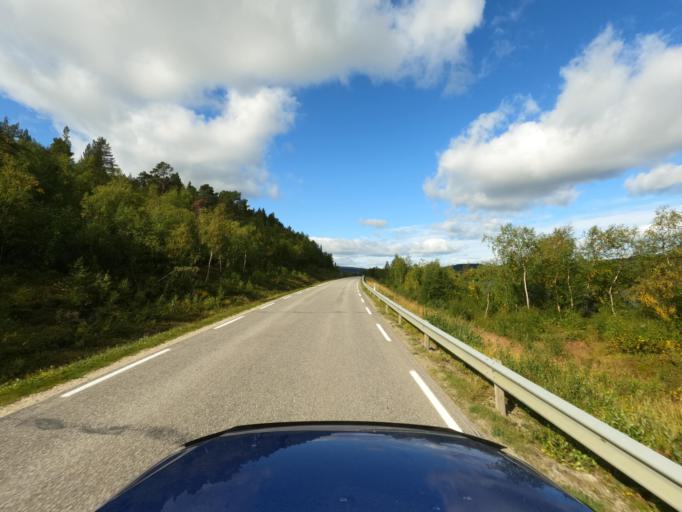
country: NO
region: Finnmark Fylke
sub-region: Karasjok
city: Karasjohka
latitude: 69.4501
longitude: 25.5855
